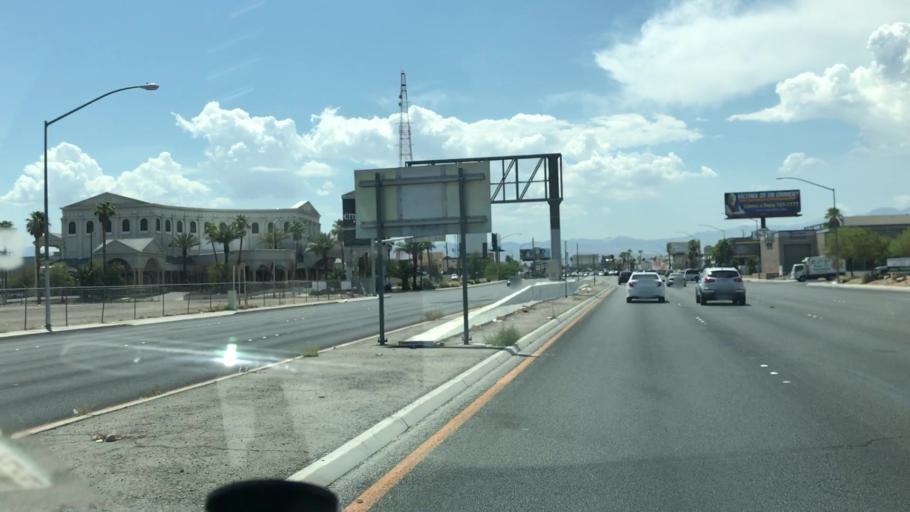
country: US
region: Nevada
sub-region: Clark County
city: Paradise
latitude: 36.1300
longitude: -115.1867
